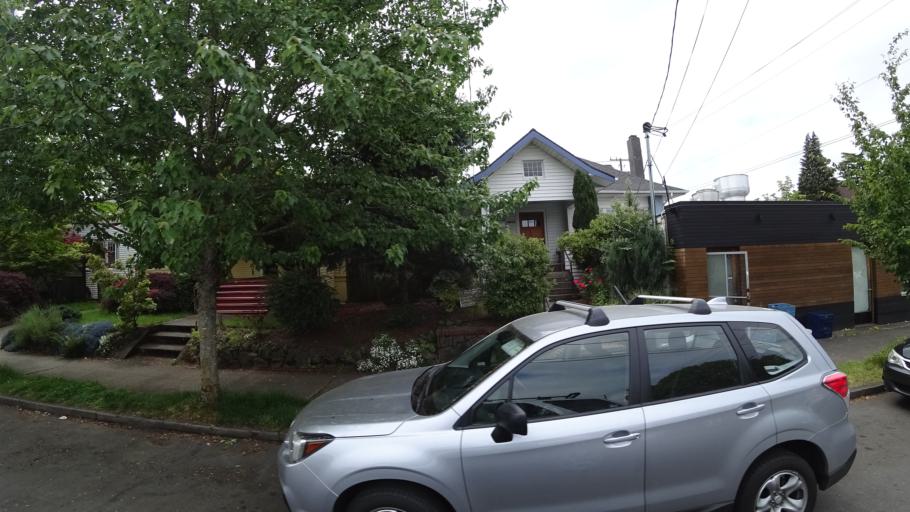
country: US
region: Oregon
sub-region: Multnomah County
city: Portland
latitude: 45.5589
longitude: -122.6409
